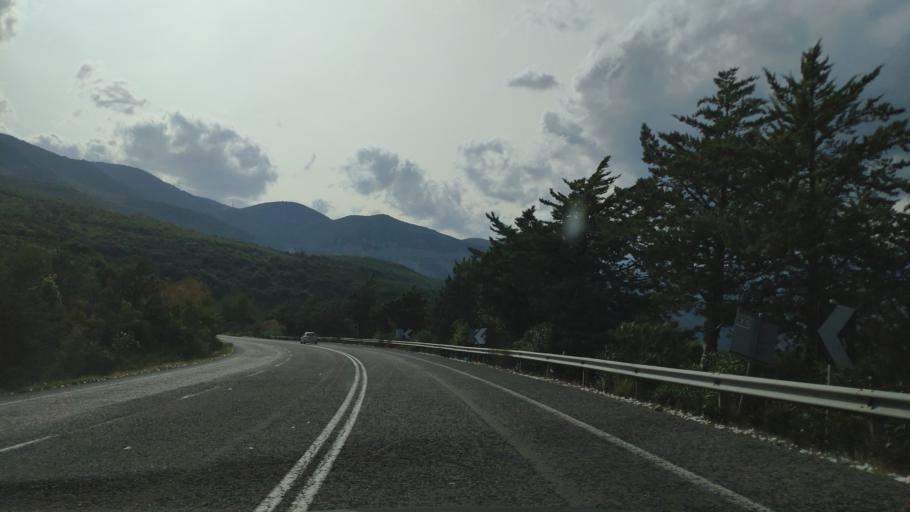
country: GR
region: Central Greece
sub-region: Nomos Fthiotidos
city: Anthili
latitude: 38.7914
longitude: 22.4891
